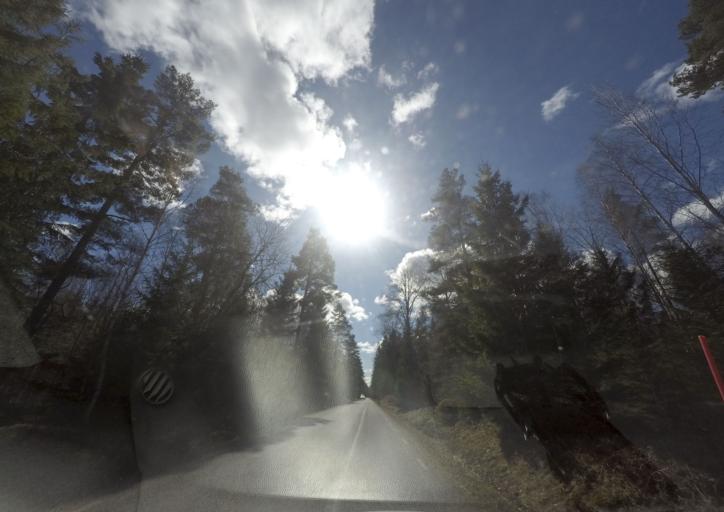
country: SE
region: OEstergoetland
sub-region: Norrkopings Kommun
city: Krokek
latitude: 58.8101
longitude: 16.4586
